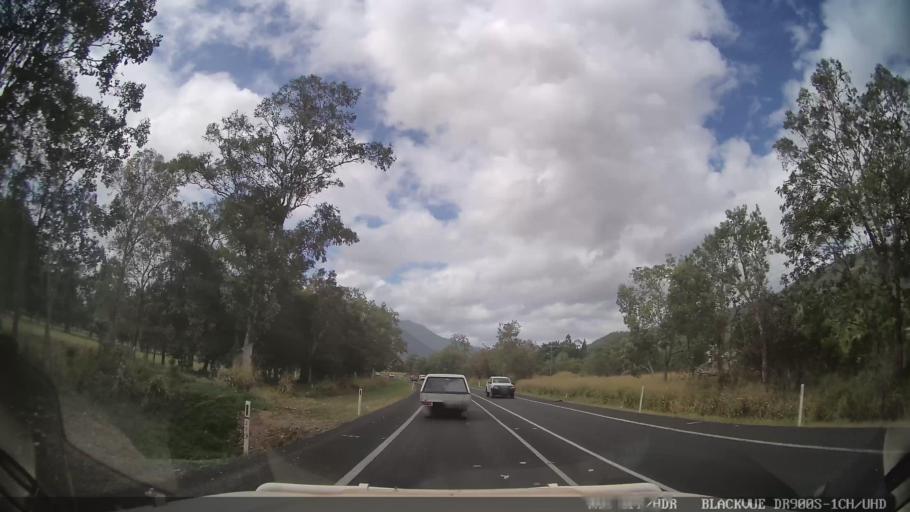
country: AU
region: Queensland
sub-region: Cairns
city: Woree
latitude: -17.0937
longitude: 145.7740
